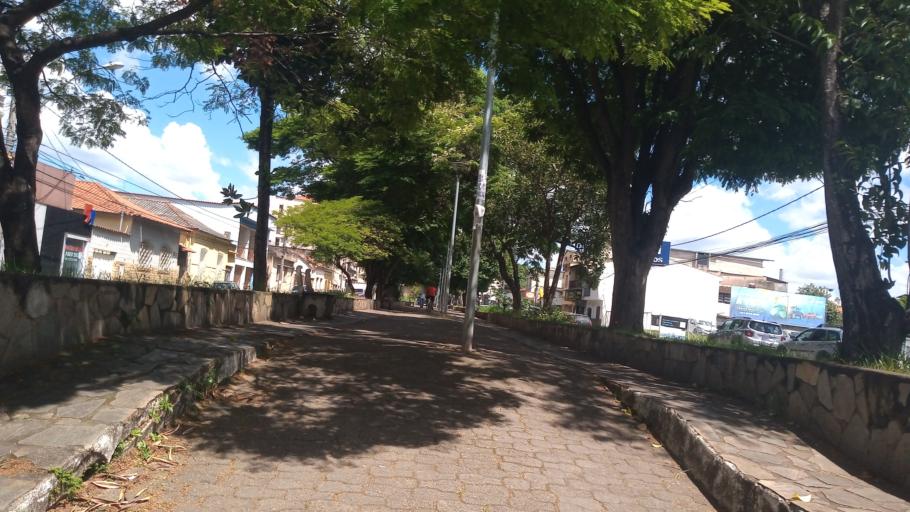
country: BR
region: Minas Gerais
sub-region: Sao Joao Del Rei
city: Sao Joao del Rei
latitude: -21.1240
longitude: -44.2478
